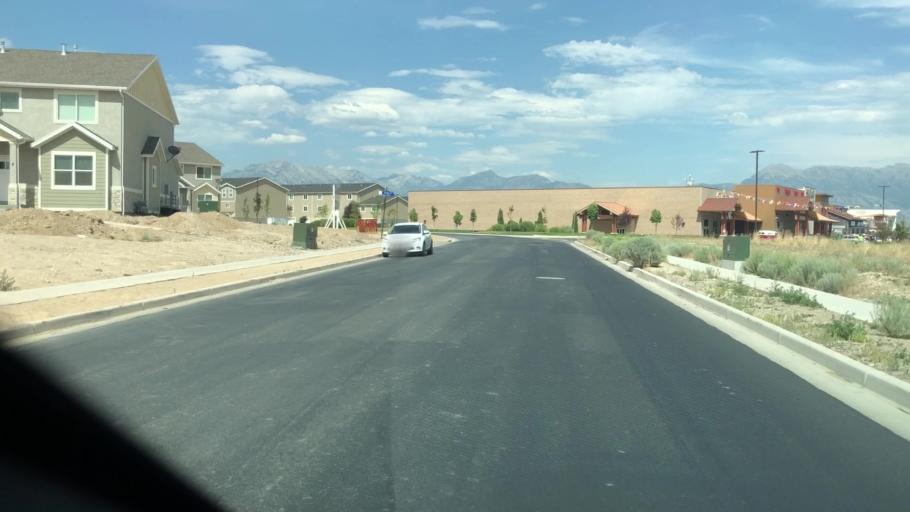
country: US
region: Utah
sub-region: Utah County
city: Eagle Mountain
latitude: 40.3634
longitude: -111.9682
